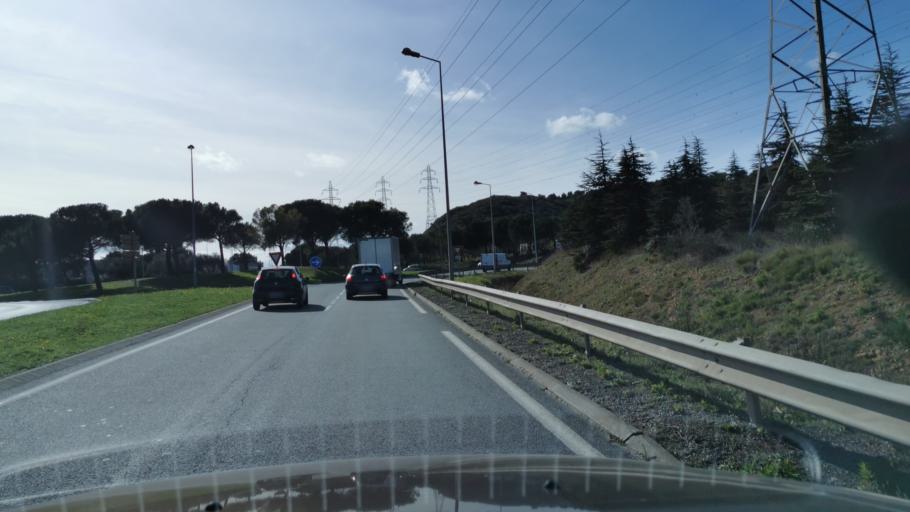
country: FR
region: Languedoc-Roussillon
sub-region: Departement de l'Aude
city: Narbonne
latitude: 43.1874
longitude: 2.9732
